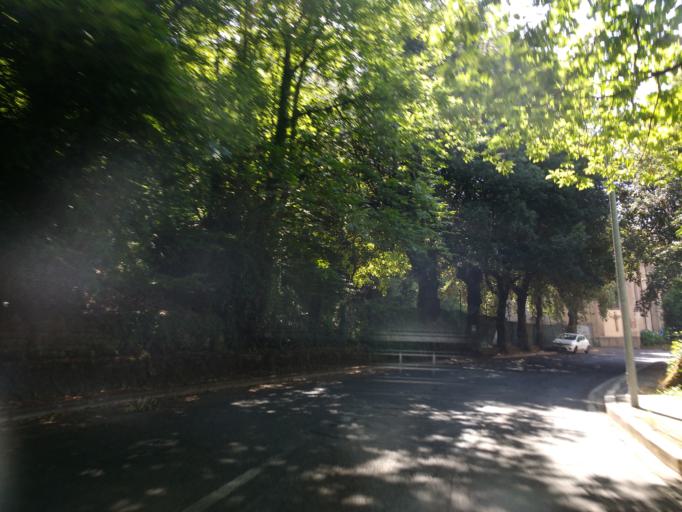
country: IT
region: Latium
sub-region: Citta metropolitana di Roma Capitale
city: Rocca di Papa
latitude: 41.7542
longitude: 12.7031
